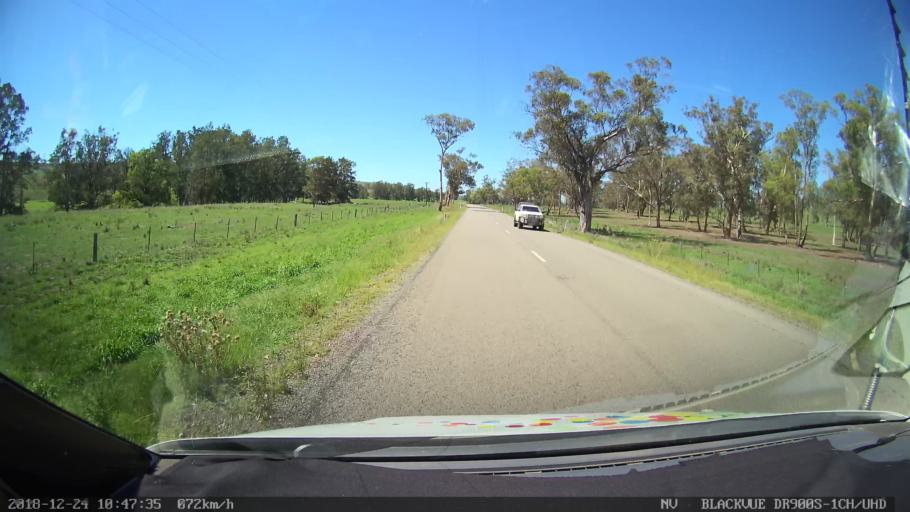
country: AU
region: New South Wales
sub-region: Upper Hunter Shire
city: Merriwa
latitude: -31.9260
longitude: 150.4297
